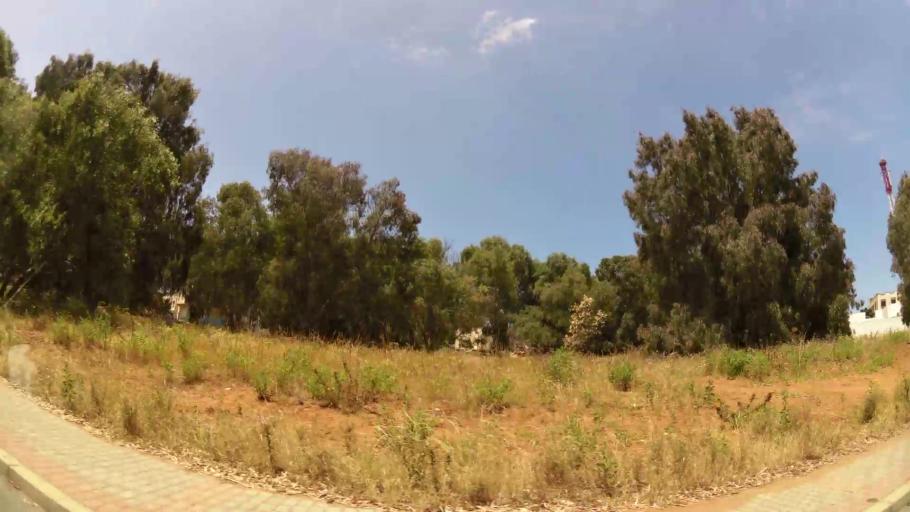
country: MA
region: Gharb-Chrarda-Beni Hssen
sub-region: Kenitra Province
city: Kenitra
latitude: 34.2627
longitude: -6.6129
